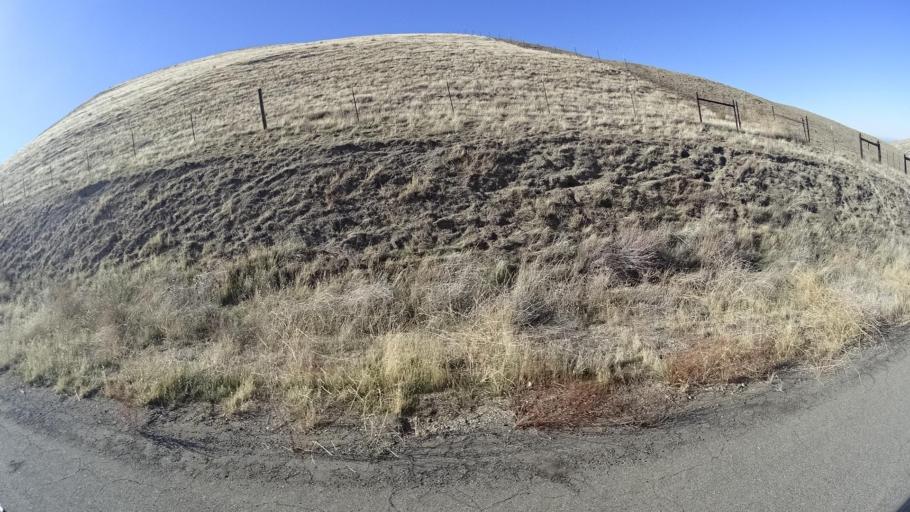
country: US
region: California
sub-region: Kern County
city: Maricopa
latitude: 34.9530
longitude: -119.4066
